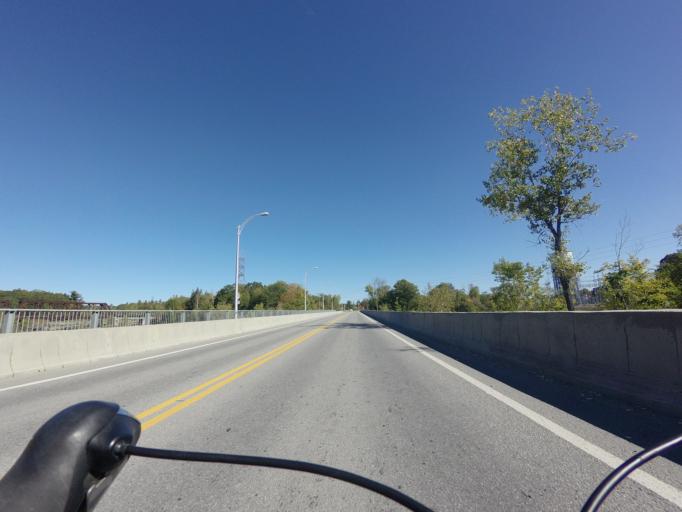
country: CA
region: Ontario
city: Clarence-Rockland
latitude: 45.5427
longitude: -75.4259
